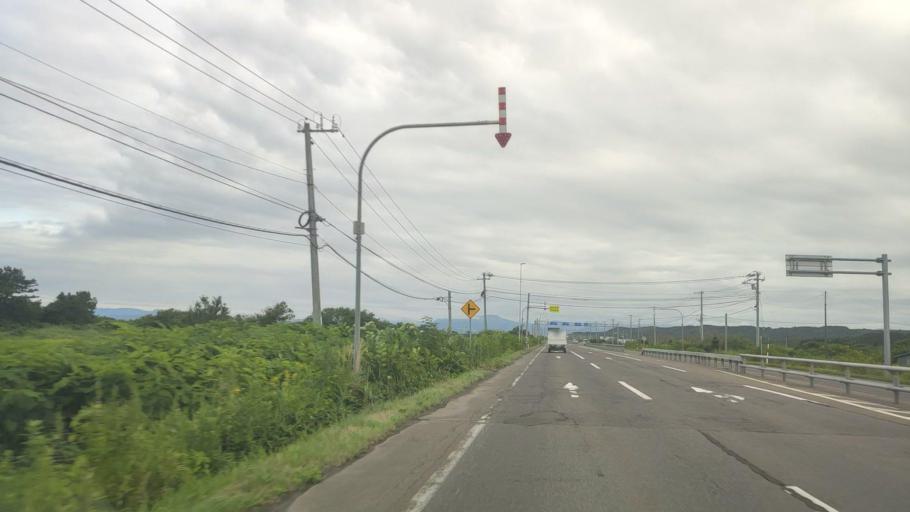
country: JP
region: Hokkaido
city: Niseko Town
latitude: 42.4059
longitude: 140.3053
